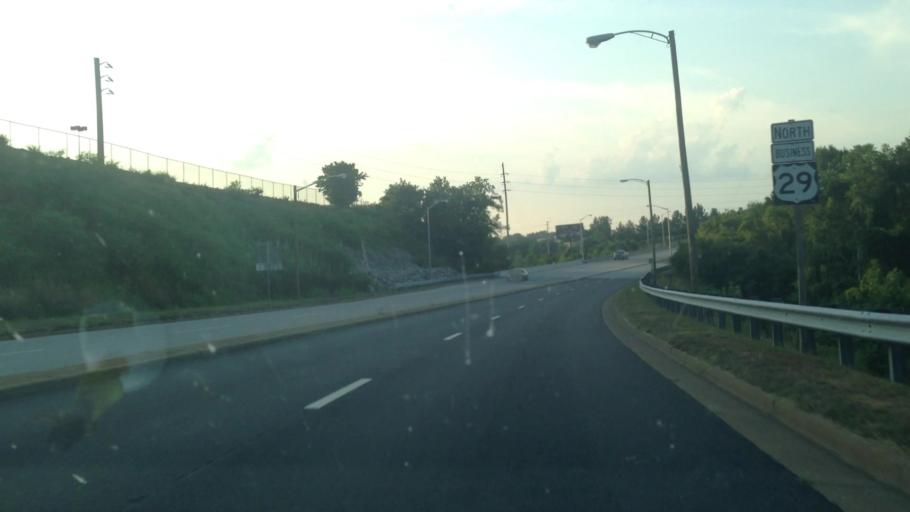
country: US
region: Virginia
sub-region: City of Danville
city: Danville
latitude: 36.5940
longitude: -79.4181
